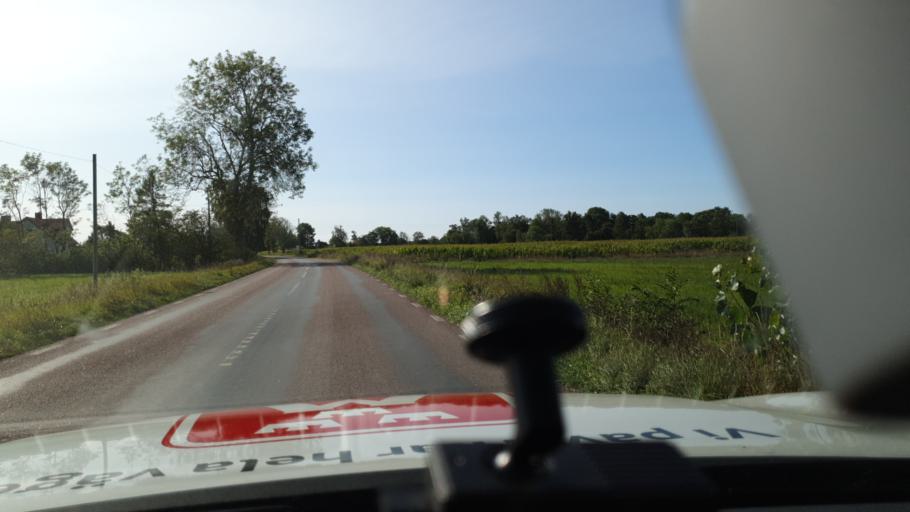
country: SE
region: Gotland
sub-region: Gotland
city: Hemse
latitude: 57.1588
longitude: 18.2811
